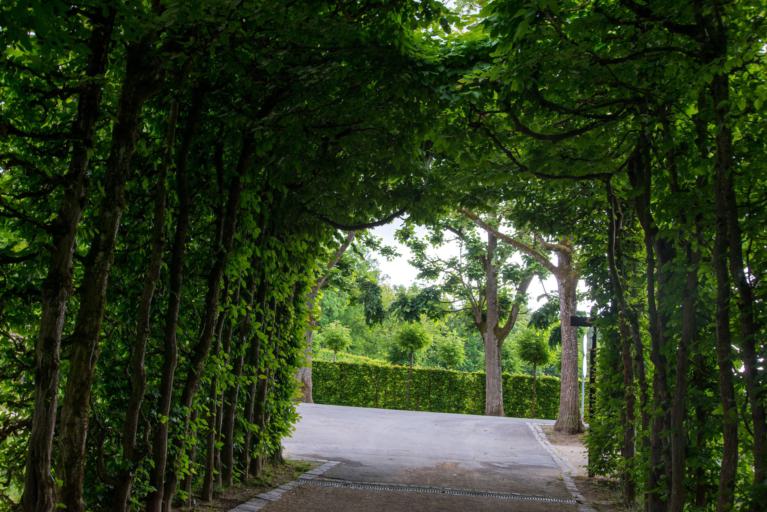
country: DE
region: Bavaria
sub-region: Upper Franconia
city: Bindlach
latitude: 49.9482
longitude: 11.6228
